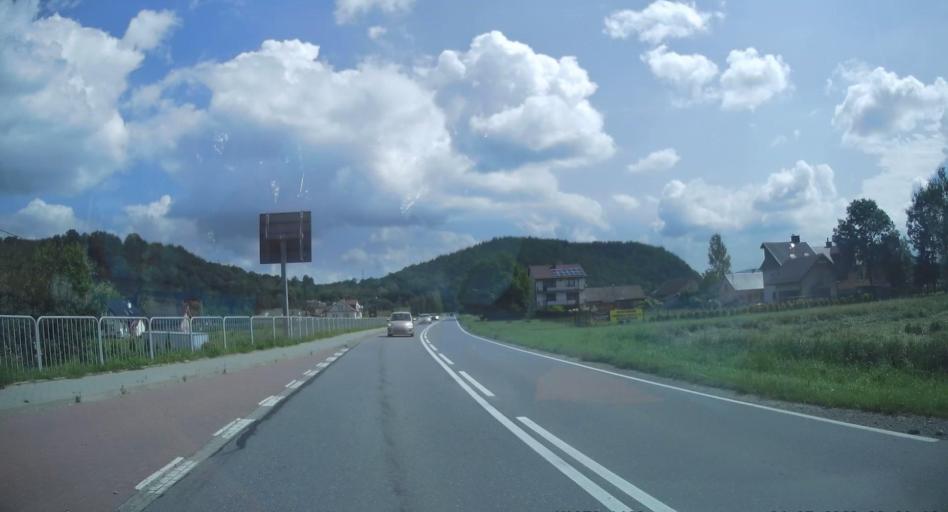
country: PL
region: Lesser Poland Voivodeship
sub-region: Powiat tarnowski
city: Zakliczyn
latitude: 49.8735
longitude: 20.8119
